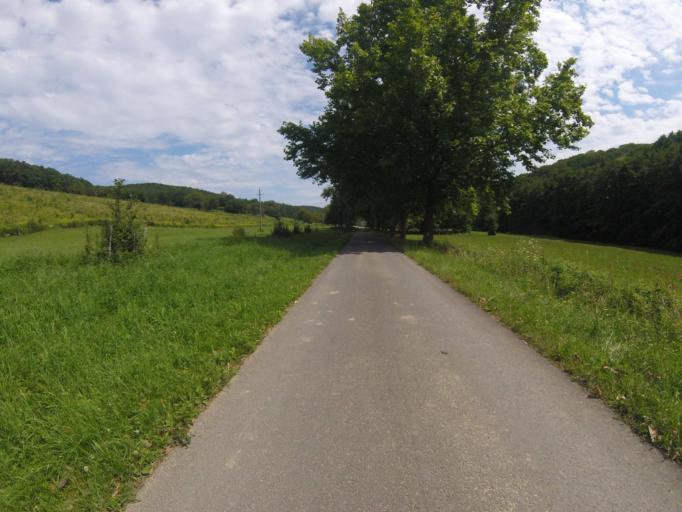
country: HU
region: Zala
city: Lenti
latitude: 46.5619
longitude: 16.6363
